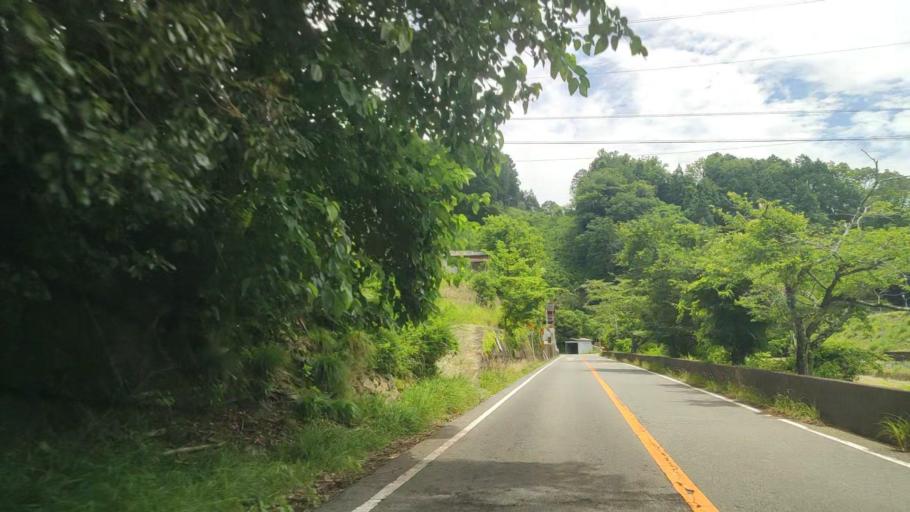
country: JP
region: Hyogo
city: Yamazakicho-nakabirose
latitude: 35.0757
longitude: 134.3595
